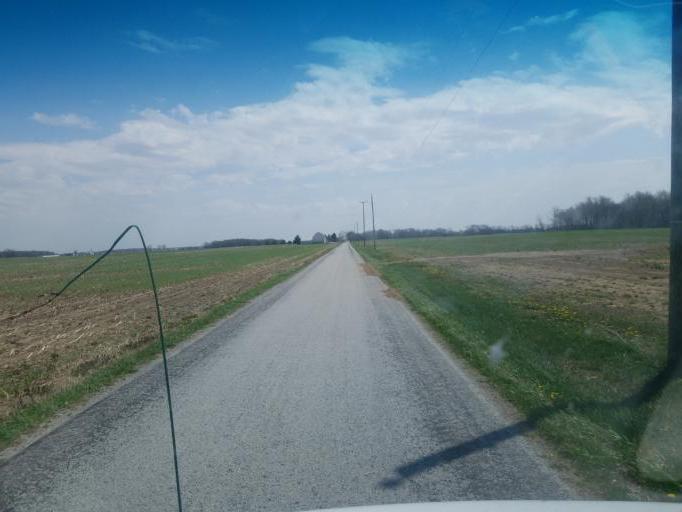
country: US
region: Ohio
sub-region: Hardin County
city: Kenton
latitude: 40.6804
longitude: -83.5556
